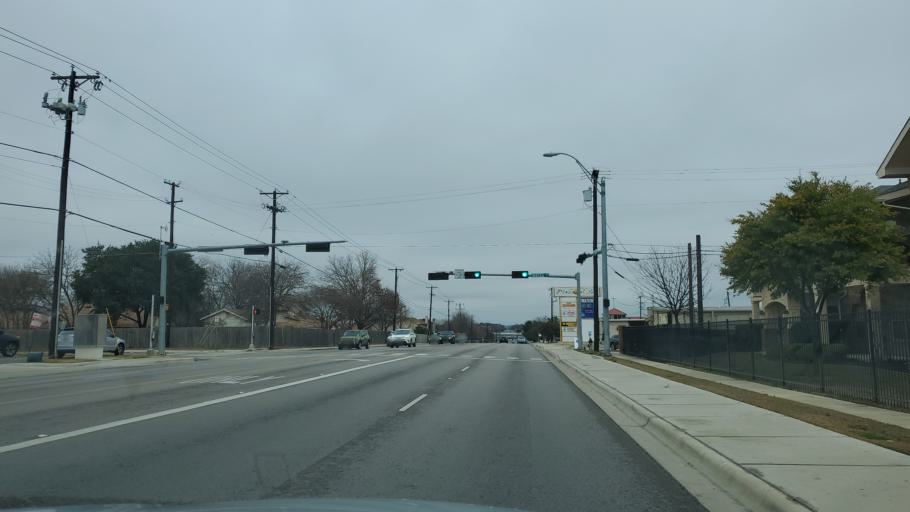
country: US
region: Texas
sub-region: Bell County
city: Killeen
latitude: 31.0851
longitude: -97.7360
